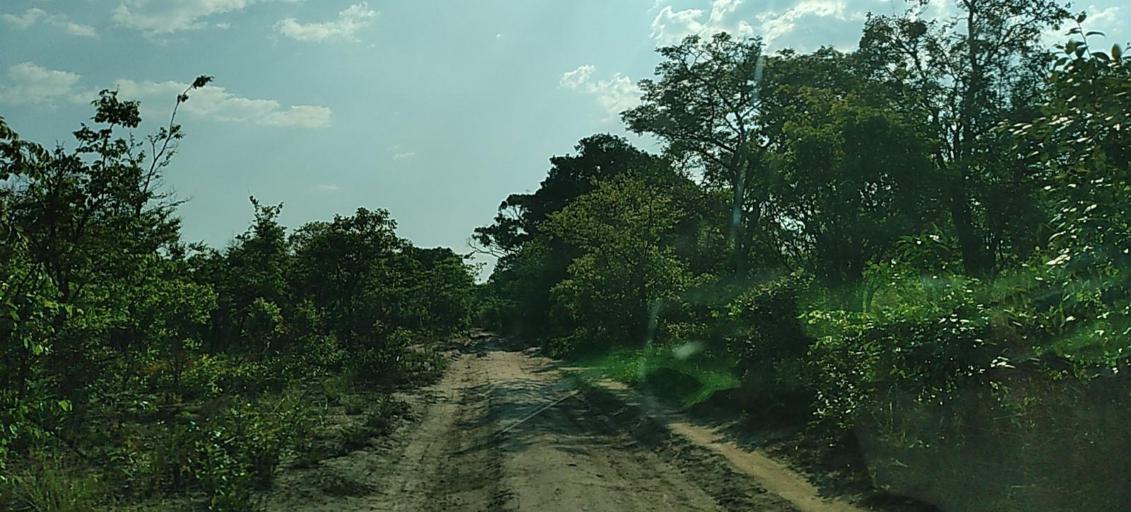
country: ZM
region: North-Western
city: Mwinilunga
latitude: -11.3150
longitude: 24.7436
